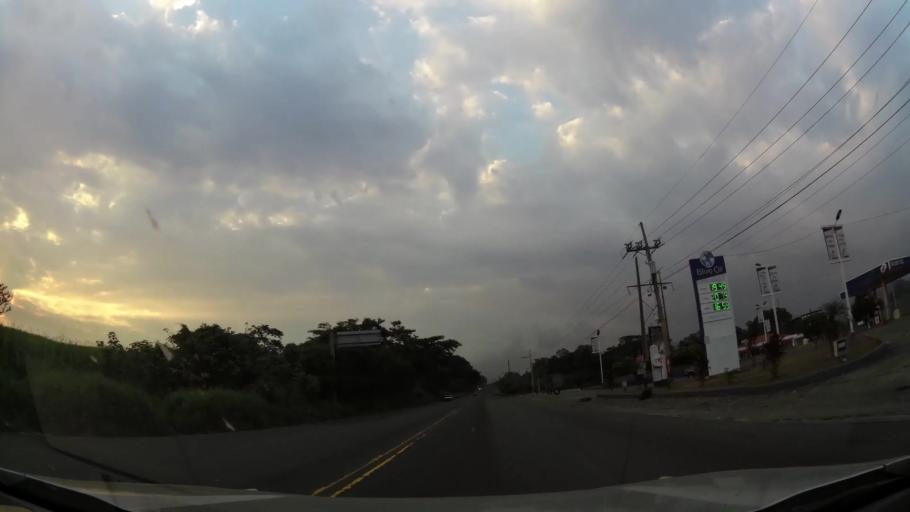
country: GT
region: Escuintla
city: Siquinala
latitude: 14.2778
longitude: -90.9203
